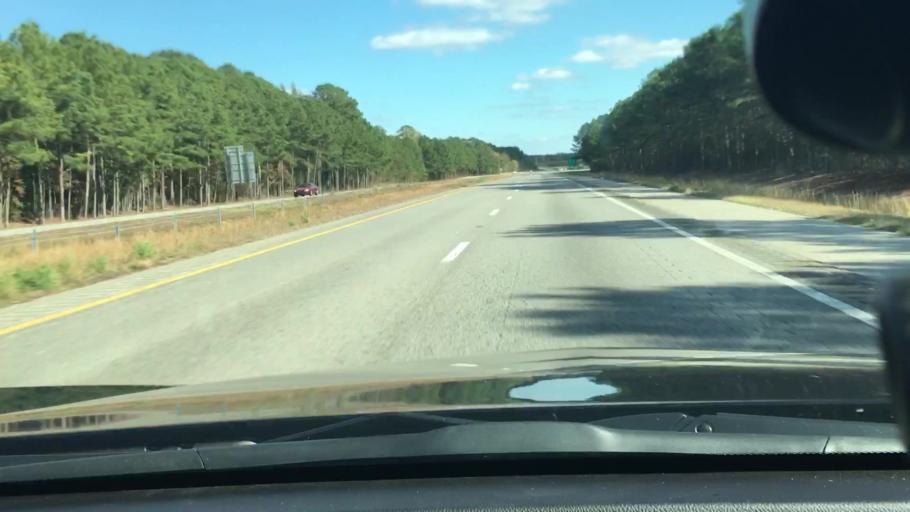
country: US
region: North Carolina
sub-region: Wilson County
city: Wilson
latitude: 35.6700
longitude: -77.7746
